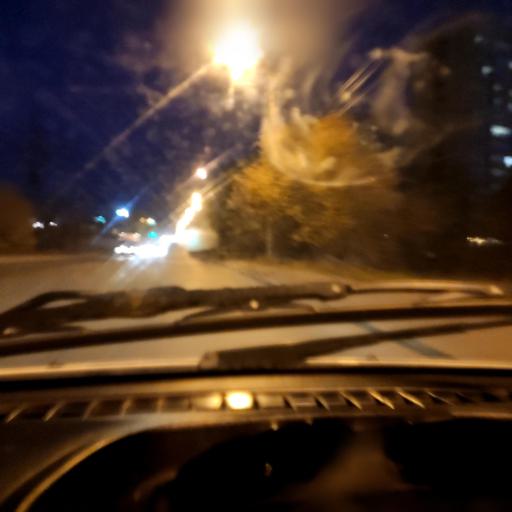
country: RU
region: Samara
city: Zhigulevsk
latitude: 53.4785
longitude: 49.5190
